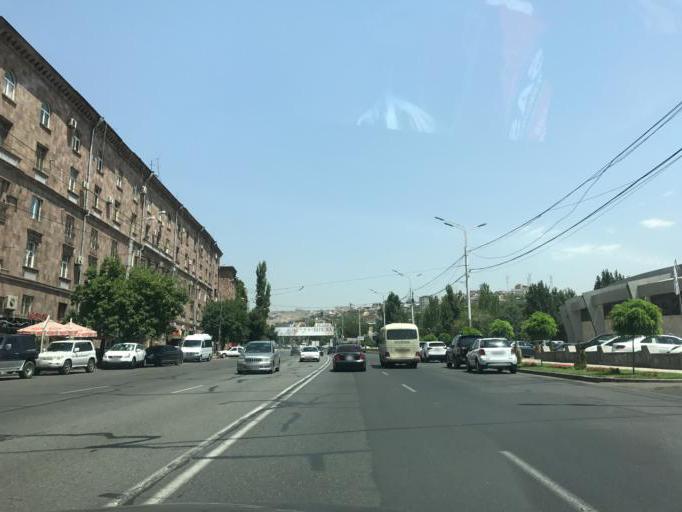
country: AM
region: Yerevan
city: Yerevan
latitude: 40.1766
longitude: 44.5219
